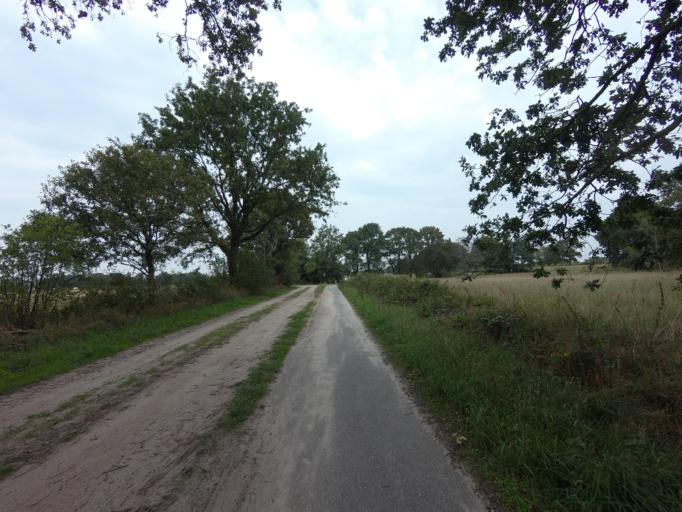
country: NL
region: Drenthe
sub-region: Gemeente Tynaarlo
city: Tynaarlo
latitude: 53.0085
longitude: 6.6338
